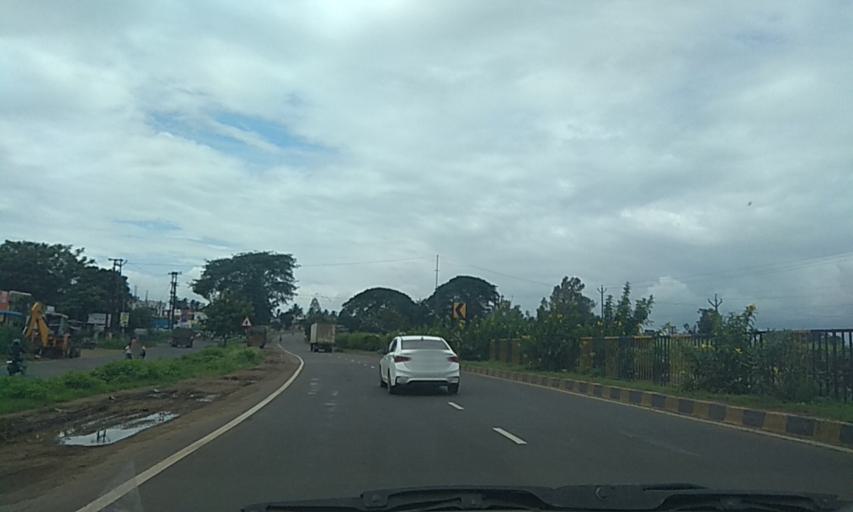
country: IN
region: Maharashtra
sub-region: Kolhapur
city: Kagal
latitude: 16.5803
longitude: 74.3118
